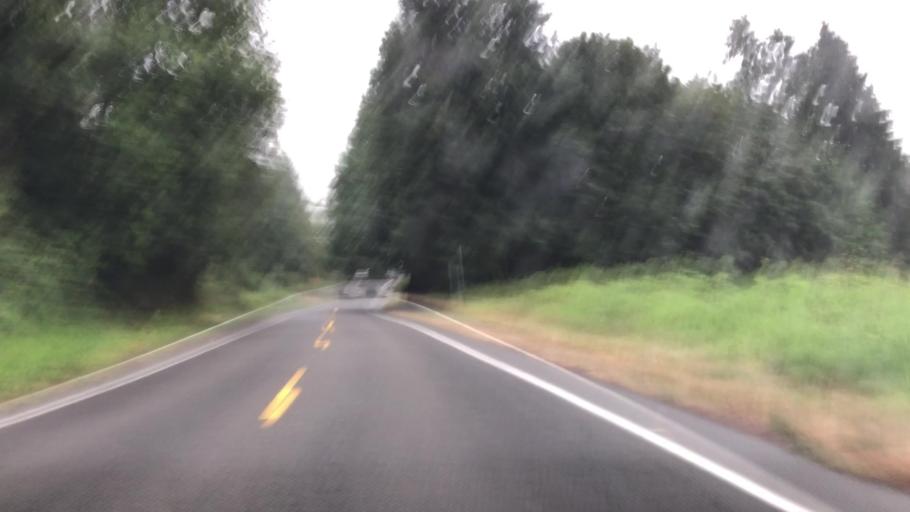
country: US
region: Washington
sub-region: King County
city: Woodinville
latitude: 47.7666
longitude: -122.1743
